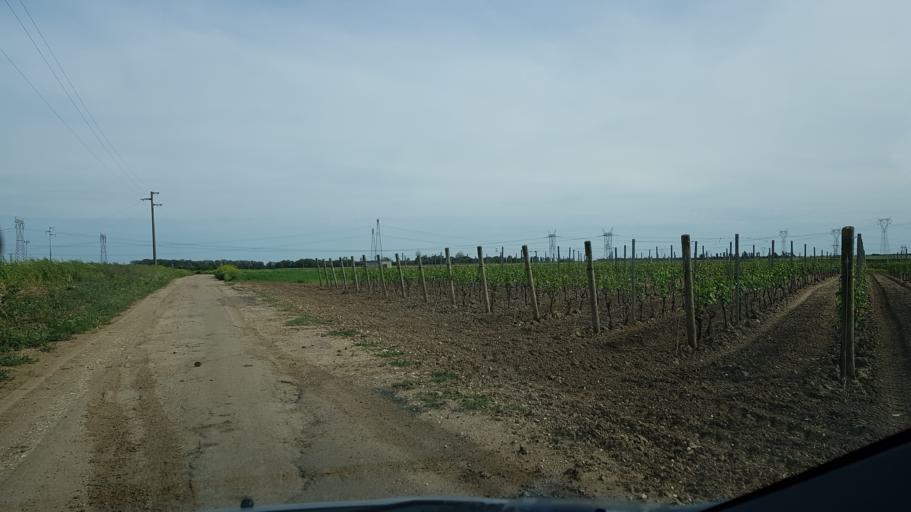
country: IT
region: Apulia
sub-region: Provincia di Brindisi
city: Tuturano
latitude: 40.5580
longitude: 17.9230
